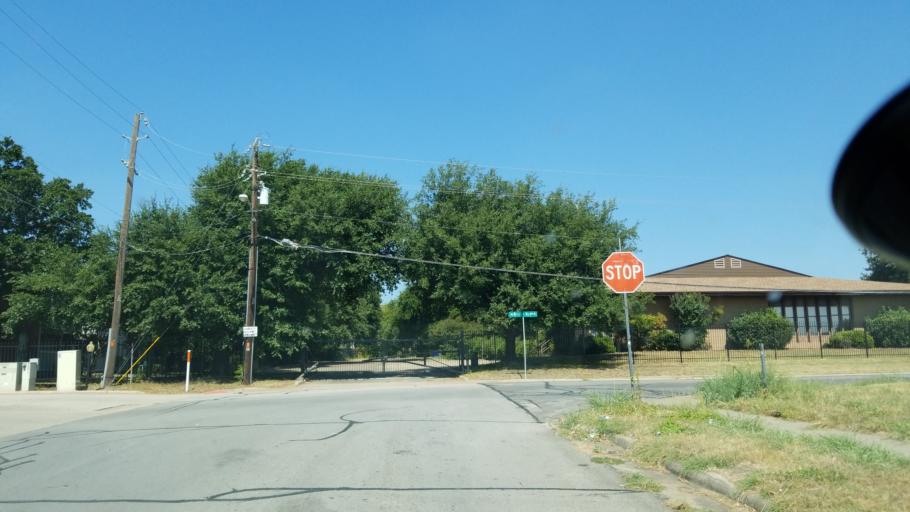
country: US
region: Texas
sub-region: Dallas County
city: Duncanville
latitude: 32.6597
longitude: -96.8842
